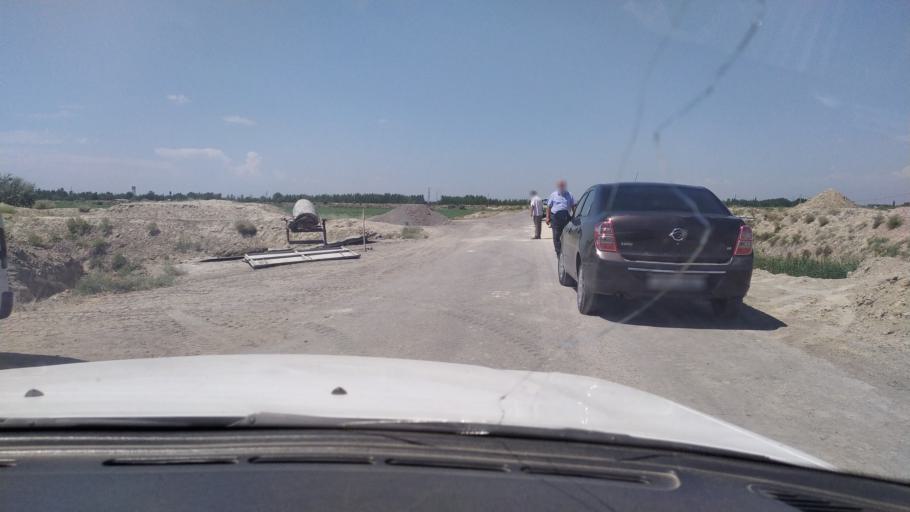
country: UZ
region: Namangan
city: Toshbuloq
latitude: 40.7905
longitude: 71.5679
